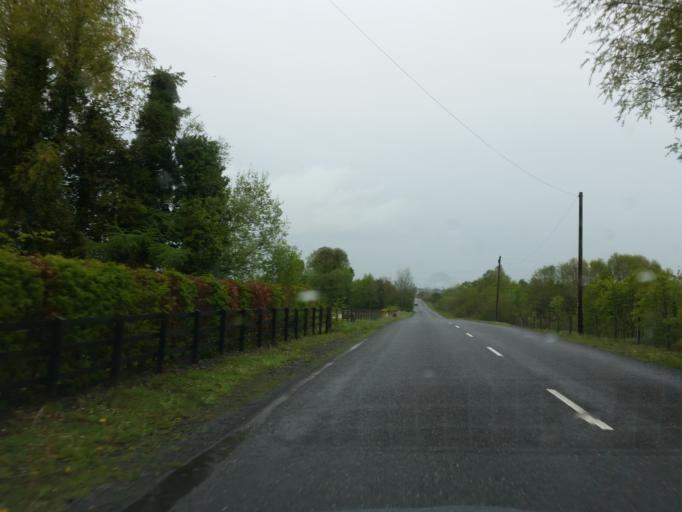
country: GB
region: Northern Ireland
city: Lisnaskea
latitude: 54.2228
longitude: -7.4613
